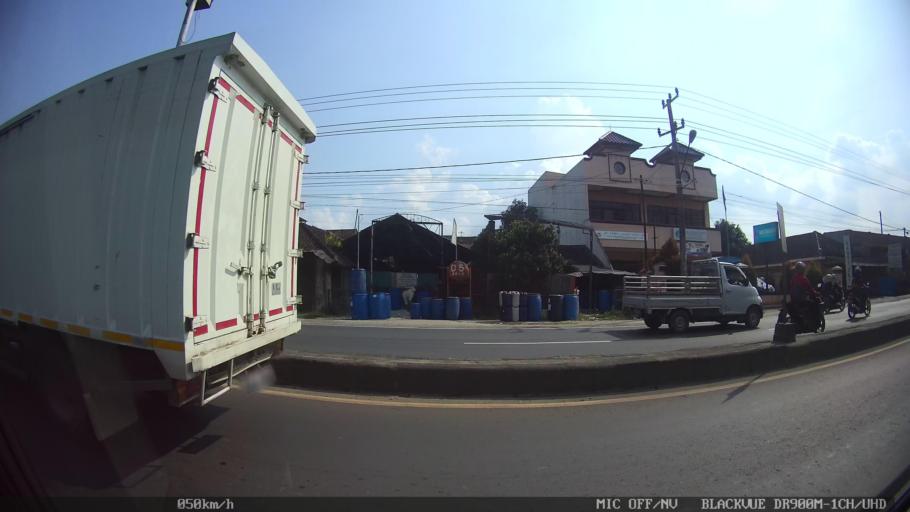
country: ID
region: Lampung
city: Natar
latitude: -5.3271
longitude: 105.2018
